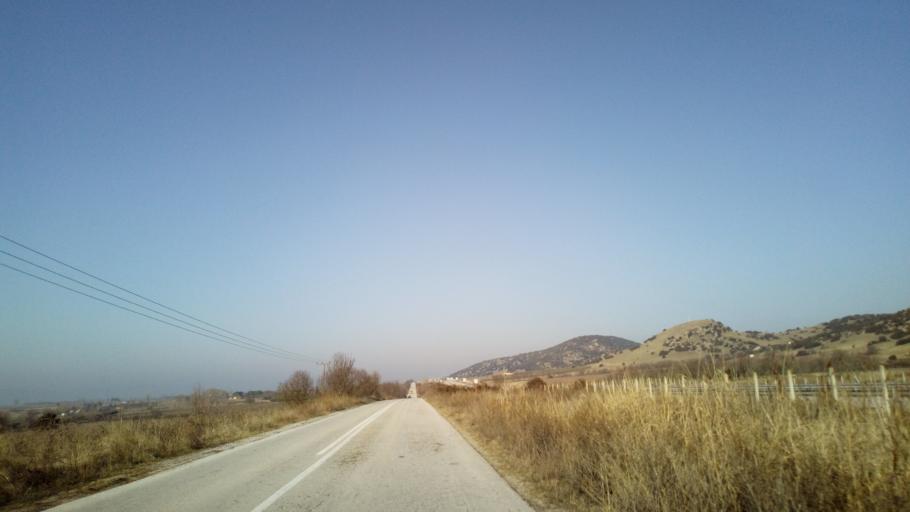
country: GR
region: Central Macedonia
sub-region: Nomos Thessalonikis
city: Gerakarou
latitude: 40.6989
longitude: 23.2063
